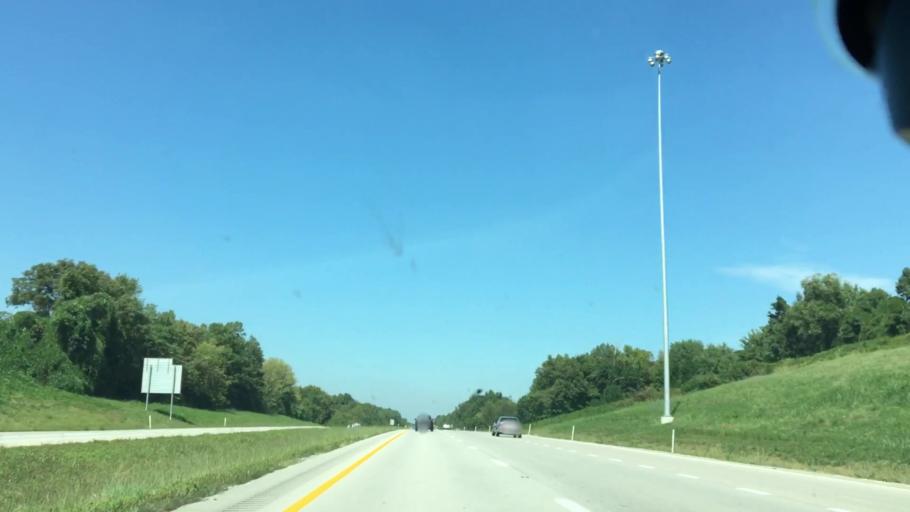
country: US
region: Kentucky
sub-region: Webster County
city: Sebree
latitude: 37.6954
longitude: -87.5143
